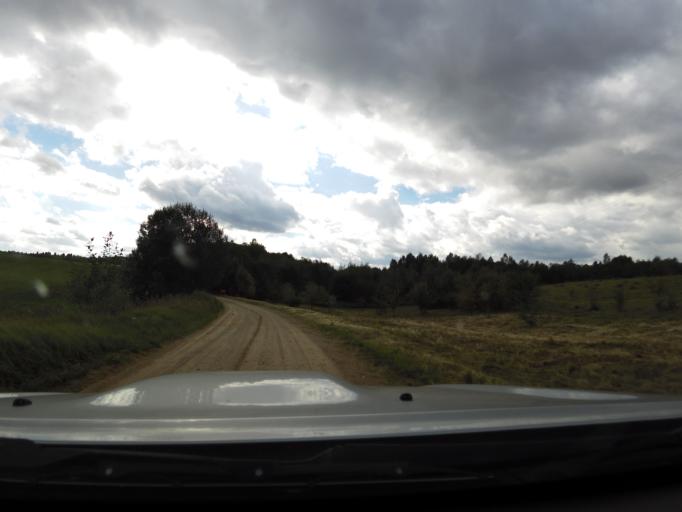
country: LT
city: Grigiskes
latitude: 54.7760
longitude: 25.0633
